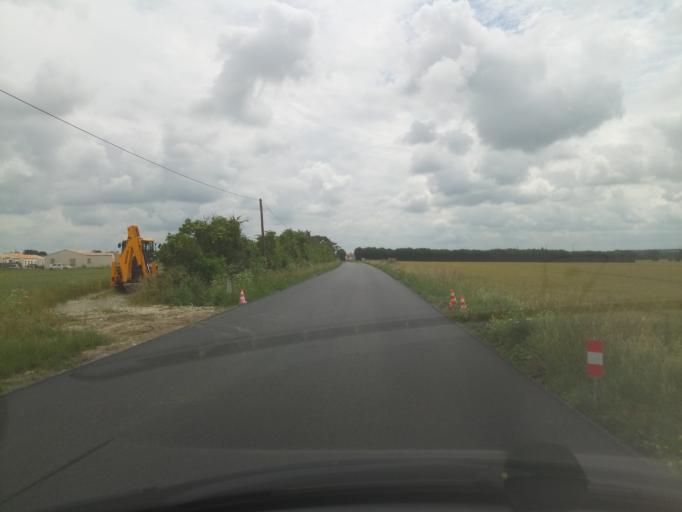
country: FR
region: Poitou-Charentes
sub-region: Departement de la Charente-Maritime
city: Saint-Jean-de-Liversay
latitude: 46.2697
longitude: -0.8867
